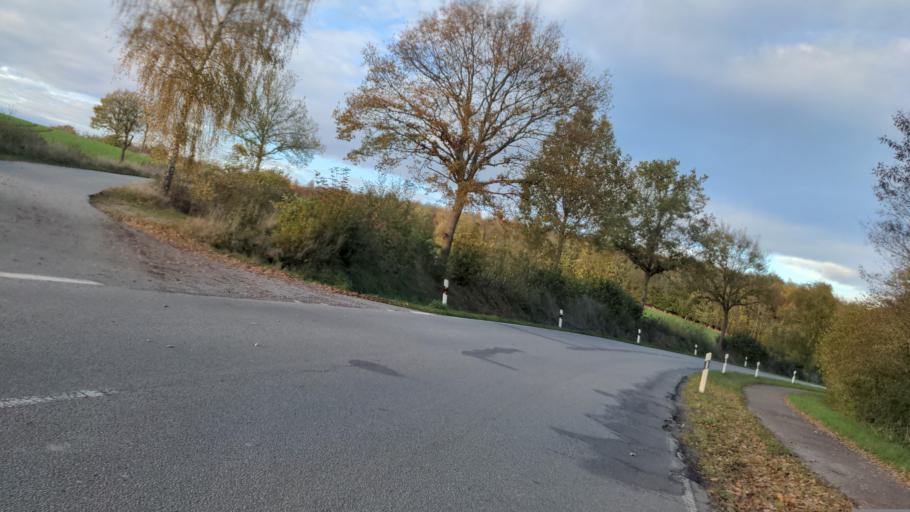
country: DE
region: Schleswig-Holstein
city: Heidekamp
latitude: 53.8564
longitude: 10.4961
